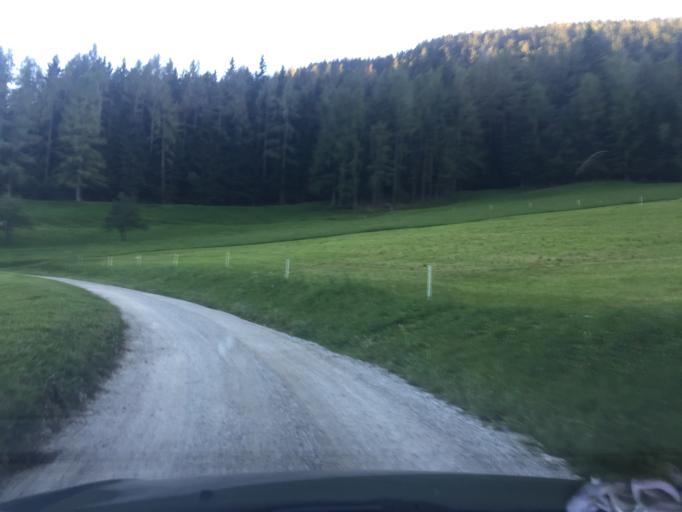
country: SI
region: Ravne na Koroskem
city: Kotlje
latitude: 46.4640
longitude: 14.9896
